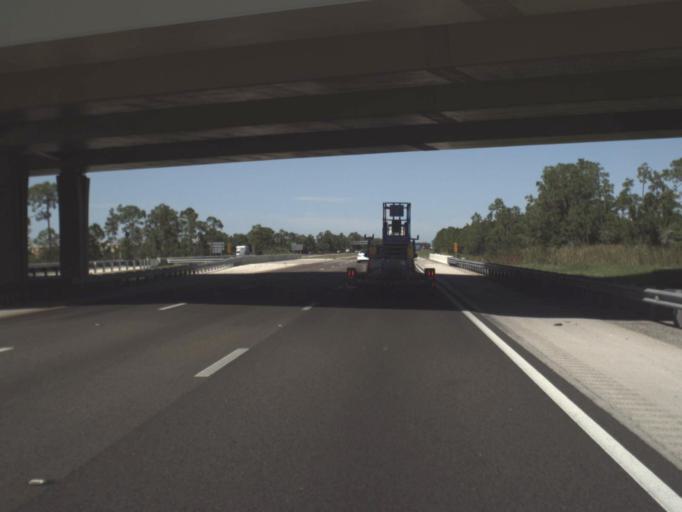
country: US
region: Florida
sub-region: Lee County
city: Three Oaks
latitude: 26.4485
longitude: -81.7835
